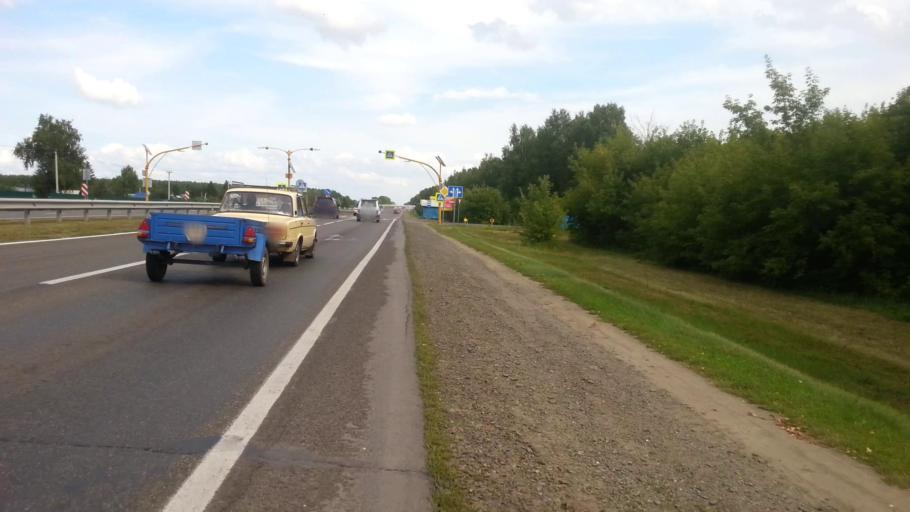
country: RU
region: Altai Krai
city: Vlasikha
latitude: 53.3545
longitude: 83.5394
